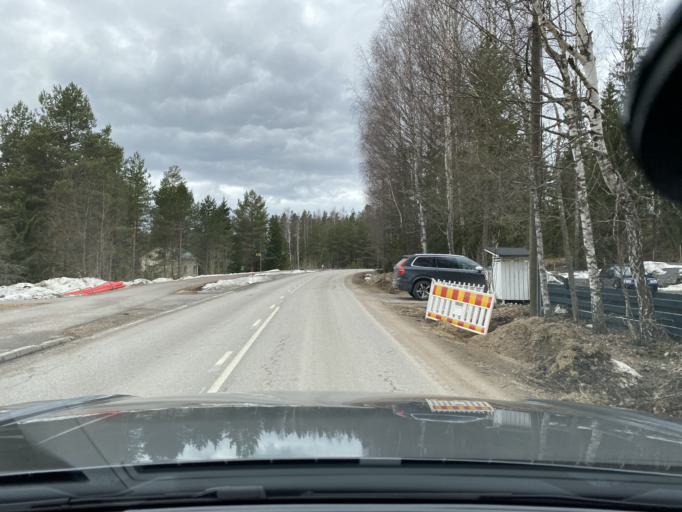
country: FI
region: Uusimaa
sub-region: Helsinki
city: Hyvinge
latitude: 60.5713
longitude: 24.7951
